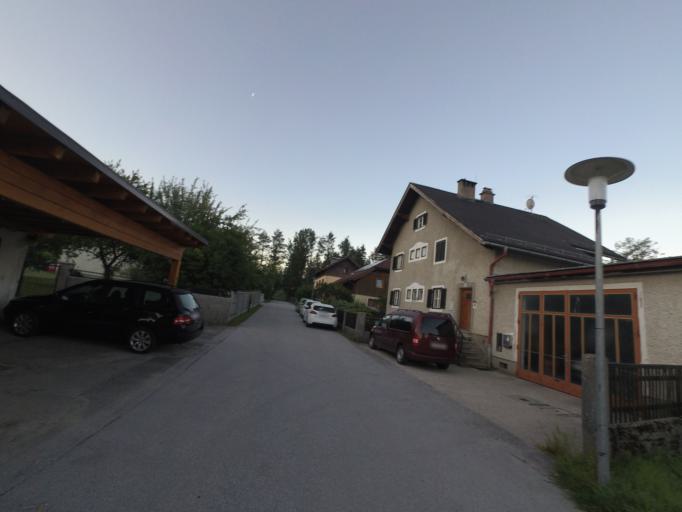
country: AT
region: Salzburg
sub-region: Politischer Bezirk Hallein
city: Puch bei Hallein
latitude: 47.7231
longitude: 13.0790
